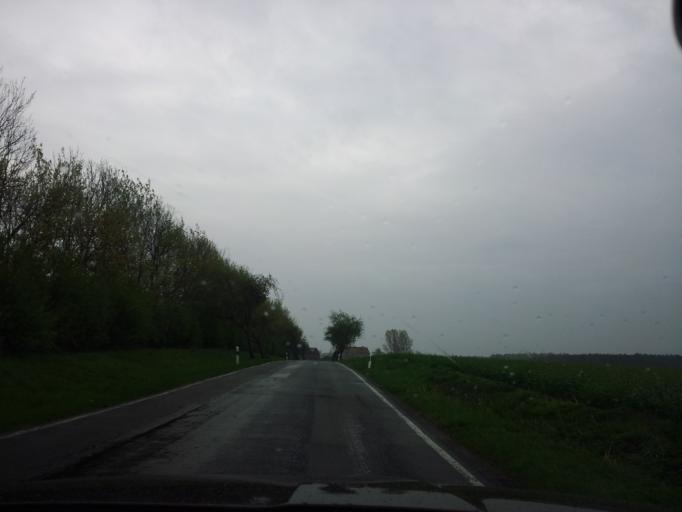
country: DE
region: Saxony-Anhalt
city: Zahna
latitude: 51.9794
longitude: 12.8246
